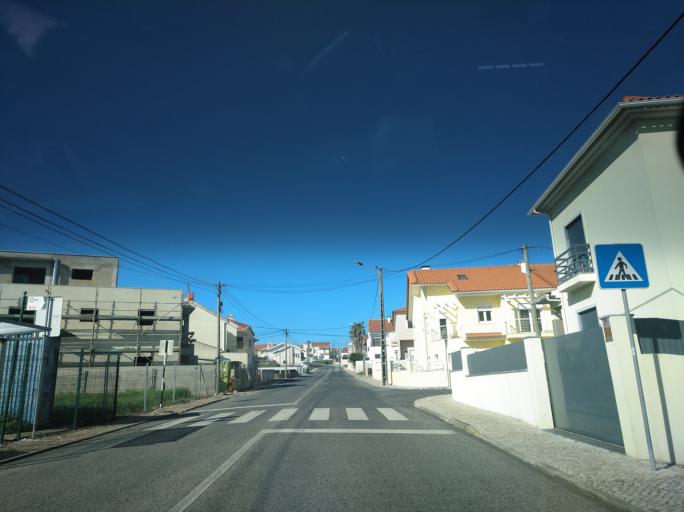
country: PT
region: Lisbon
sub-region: Odivelas
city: Canecas
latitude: 38.8017
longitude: -9.2175
